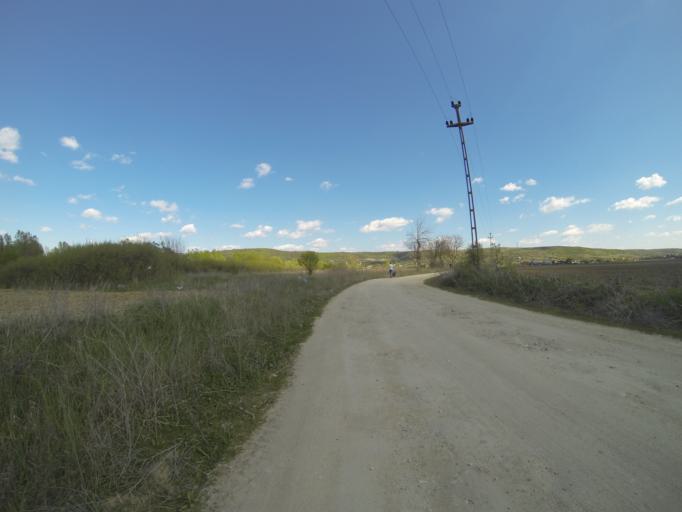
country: RO
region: Dolj
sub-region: Comuna Goesti
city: Goesti
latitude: 44.4998
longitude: 23.7463
